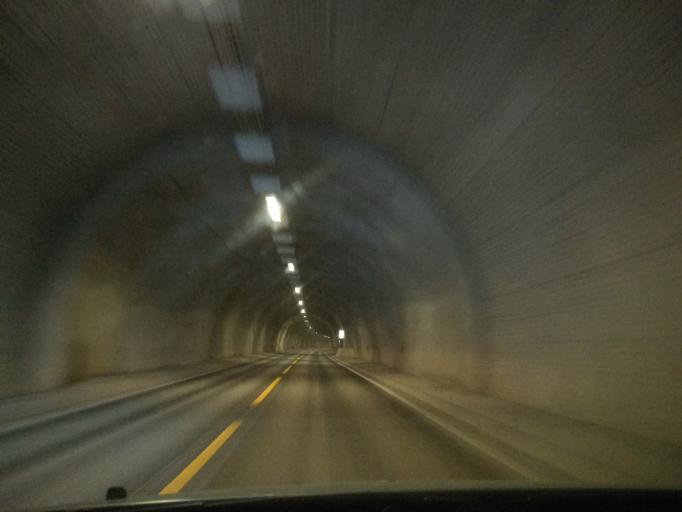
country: NO
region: Rogaland
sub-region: Sauda
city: Sauda
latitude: 59.8315
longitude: 6.2751
